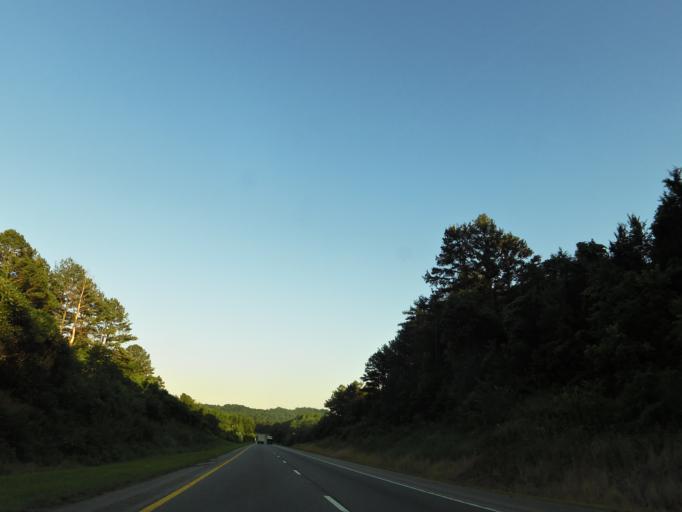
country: US
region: Tennessee
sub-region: Smith County
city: Gordonsville
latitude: 36.1544
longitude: -85.8783
